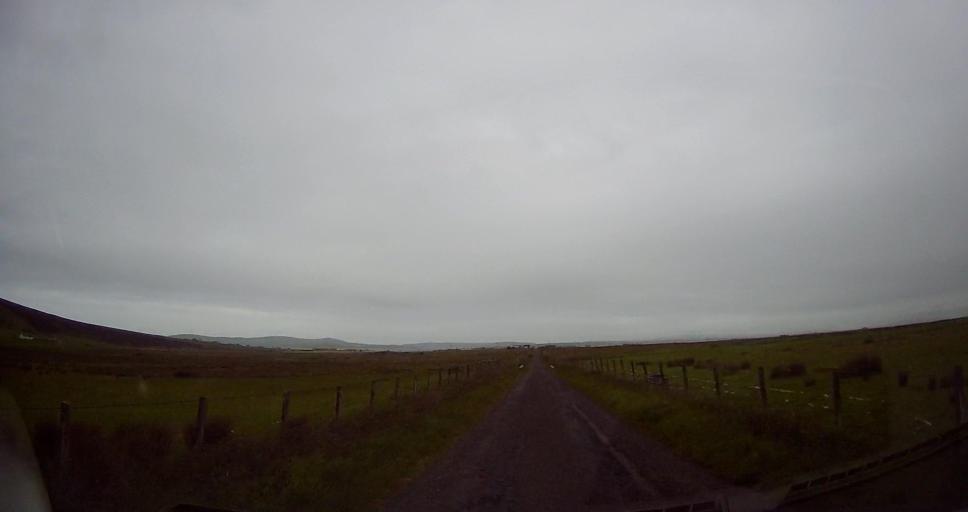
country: GB
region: Scotland
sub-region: Orkney Islands
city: Stromness
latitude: 58.9802
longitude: -3.1777
